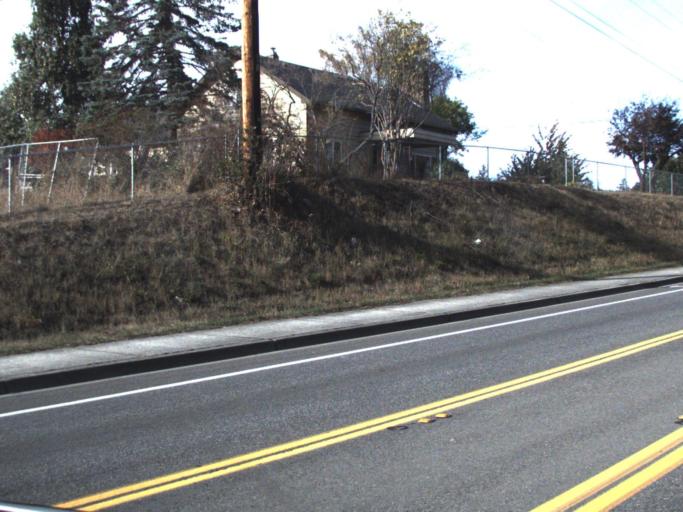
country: US
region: Washington
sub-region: Island County
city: Oak Harbor
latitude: 48.2770
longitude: -122.6696
